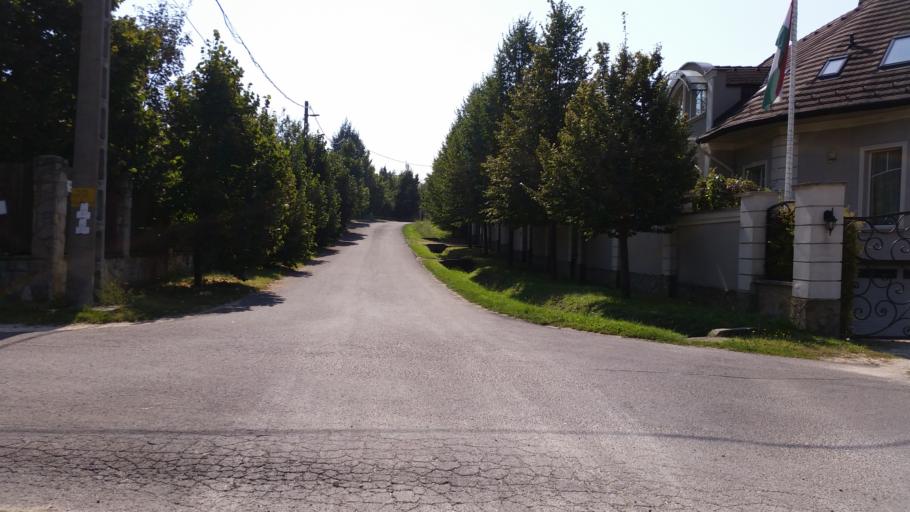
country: HU
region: Pest
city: Telki
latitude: 47.5532
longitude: 18.8257
